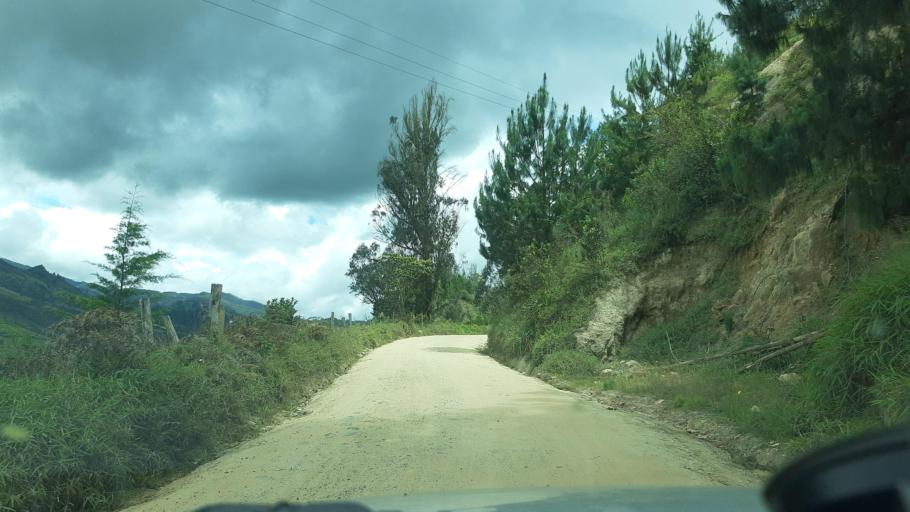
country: CO
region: Cundinamarca
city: Umbita
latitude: 5.2195
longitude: -73.4435
